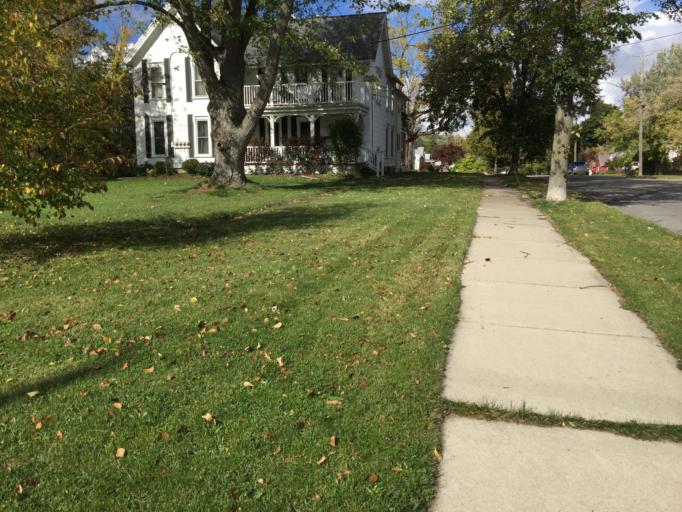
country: US
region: New York
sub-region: Erie County
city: Hamburg
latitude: 42.7154
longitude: -78.8210
